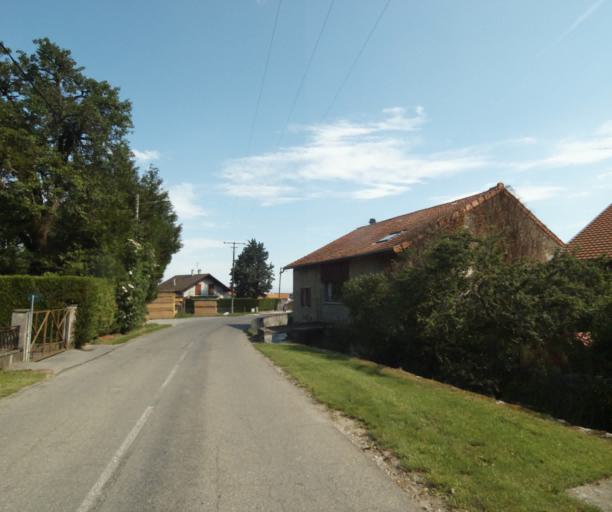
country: FR
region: Rhone-Alpes
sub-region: Departement de la Haute-Savoie
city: Lyaud
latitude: 46.3194
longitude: 6.4987
